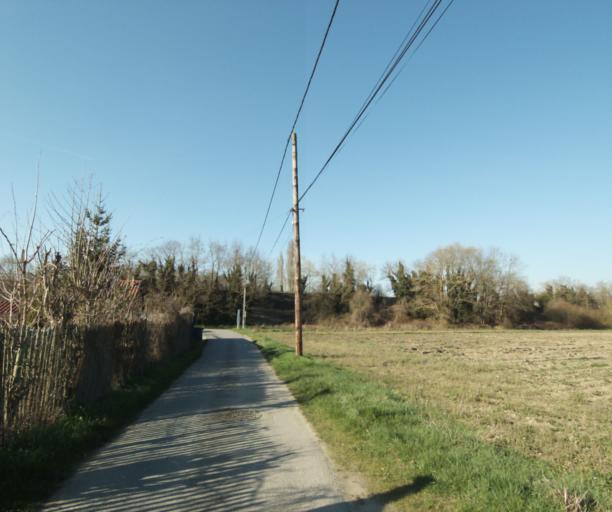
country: FR
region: Ile-de-France
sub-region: Departement du Val-d'Oise
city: Neuville-sur-Oise
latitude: 49.0267
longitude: 2.0652
